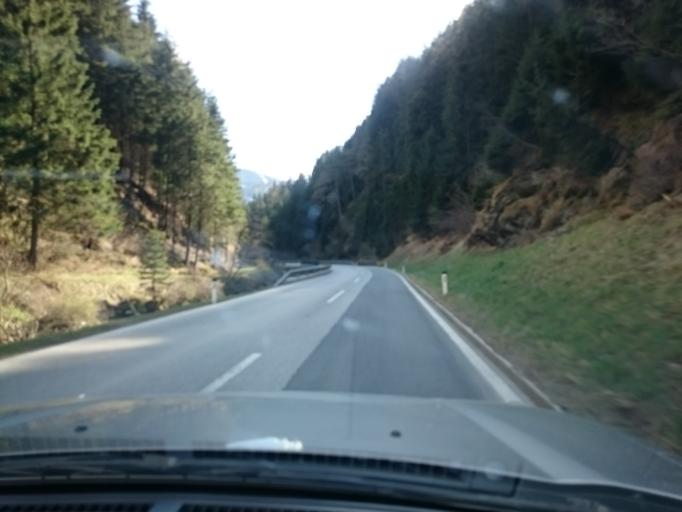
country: AT
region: Tyrol
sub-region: Politischer Bezirk Innsbruck Land
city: Gries am Brenner
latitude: 47.0485
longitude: 11.4842
